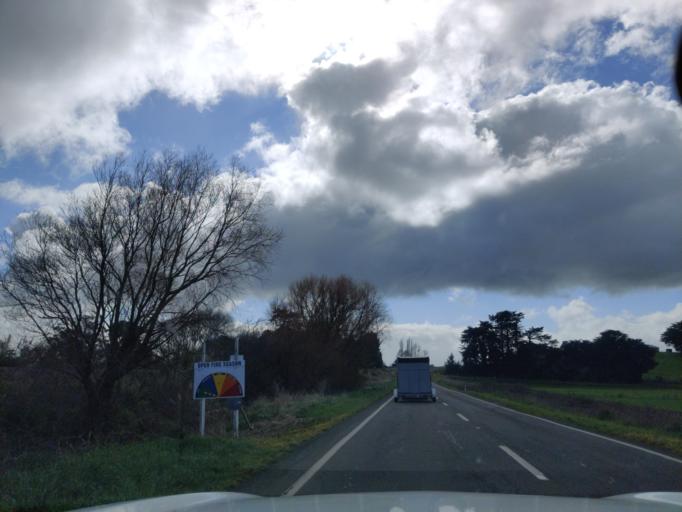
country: NZ
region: Manawatu-Wanganui
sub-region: Palmerston North City
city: Palmerston North
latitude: -40.4575
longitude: 175.5175
